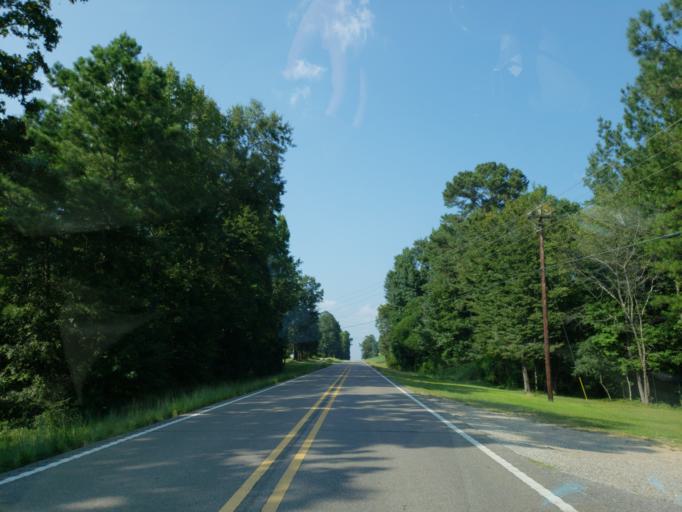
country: US
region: Mississippi
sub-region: Clarke County
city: Stonewall
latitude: 32.2282
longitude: -88.7723
